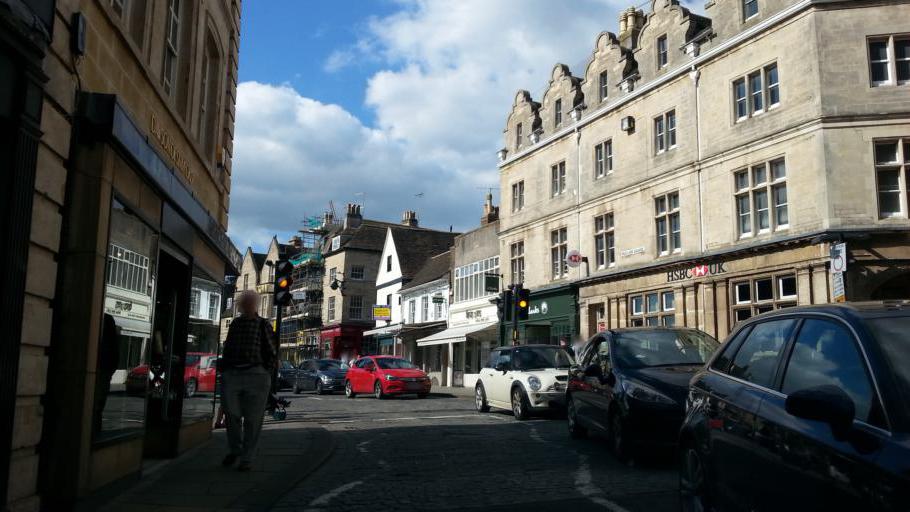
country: GB
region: England
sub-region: Lincolnshire
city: Stamford
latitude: 52.6518
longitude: -0.4801
